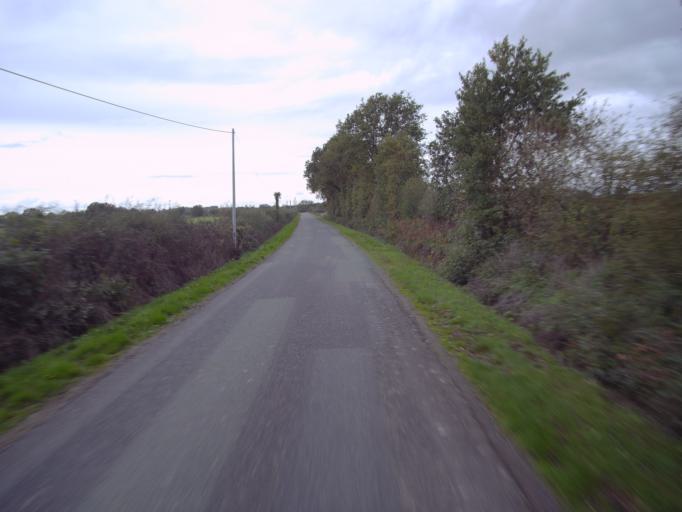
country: FR
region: Pays de la Loire
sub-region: Departement de la Loire-Atlantique
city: Remouille
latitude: 47.0196
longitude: -1.3807
